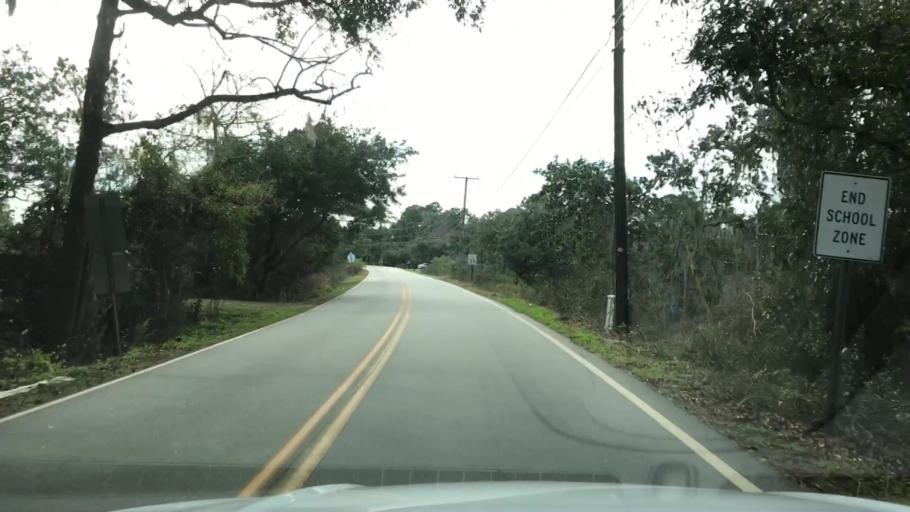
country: US
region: South Carolina
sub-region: Charleston County
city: Shell Point
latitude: 32.7785
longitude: -80.0195
